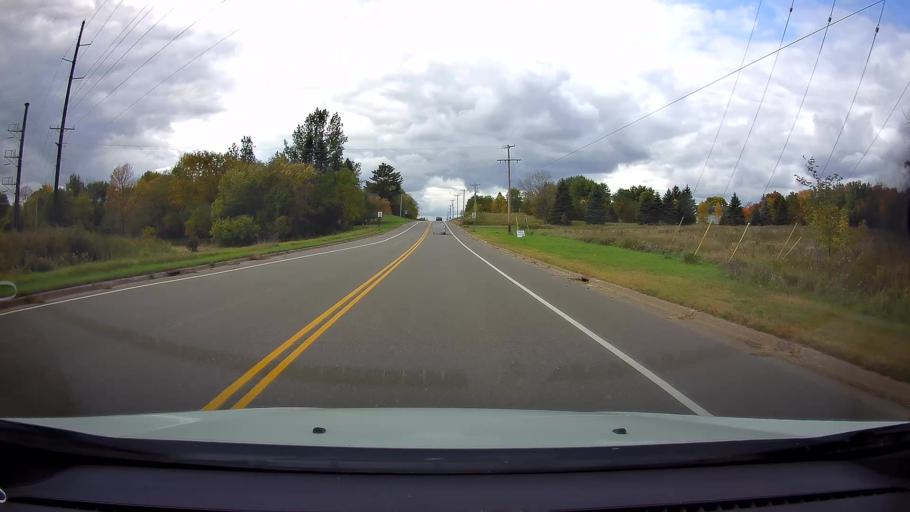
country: US
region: Minnesota
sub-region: Chisago County
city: Center City
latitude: 45.3973
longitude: -92.8063
